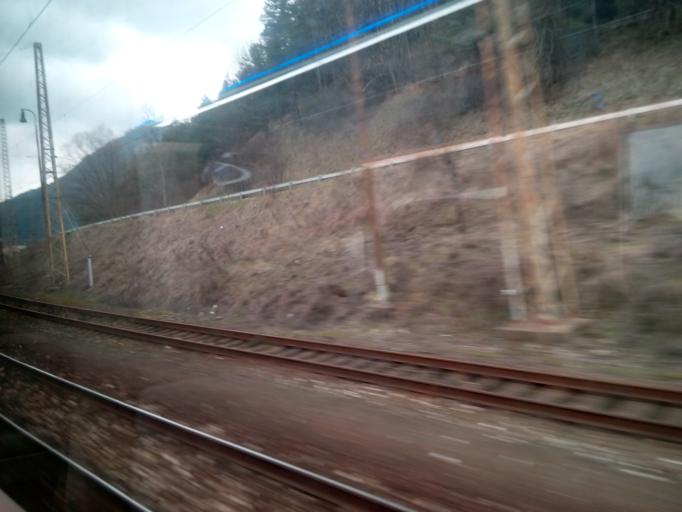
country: SK
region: Zilinsky
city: Ruzomberok
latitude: 49.0812
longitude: 19.3145
